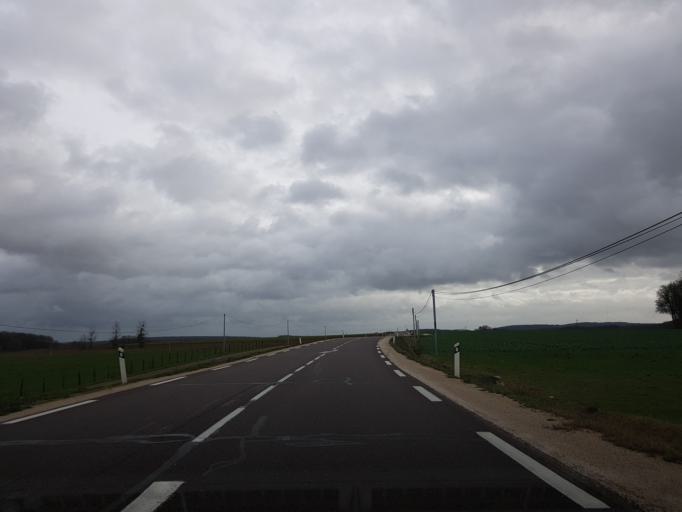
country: FR
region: Champagne-Ardenne
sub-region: Departement de la Haute-Marne
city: Fayl-Billot
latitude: 47.7668
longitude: 5.7086
